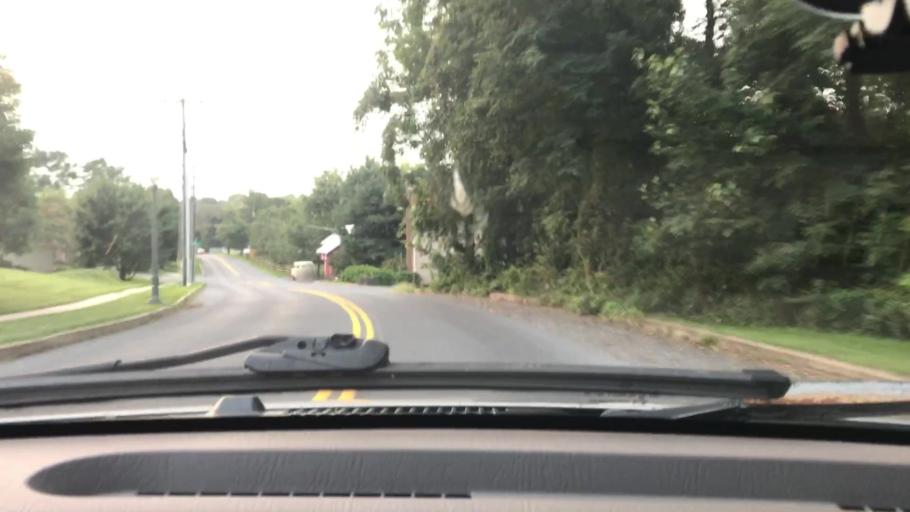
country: US
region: Pennsylvania
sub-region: Lancaster County
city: Elizabethtown
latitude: 40.1669
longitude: -76.5937
